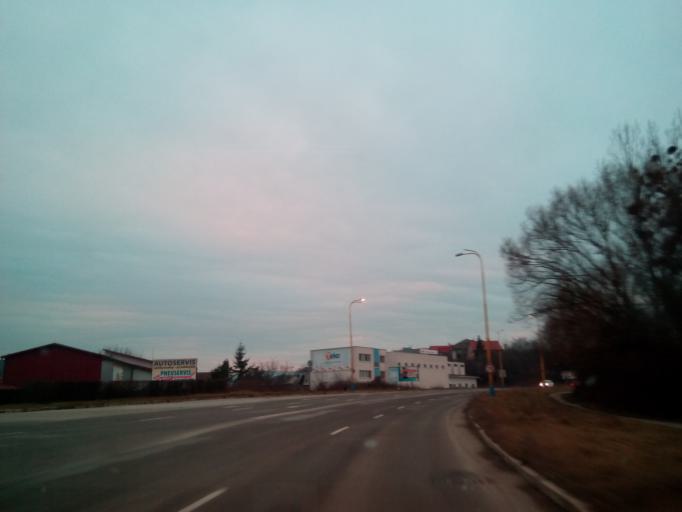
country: SK
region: Kosicky
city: Kosice
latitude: 48.7017
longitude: 21.2203
